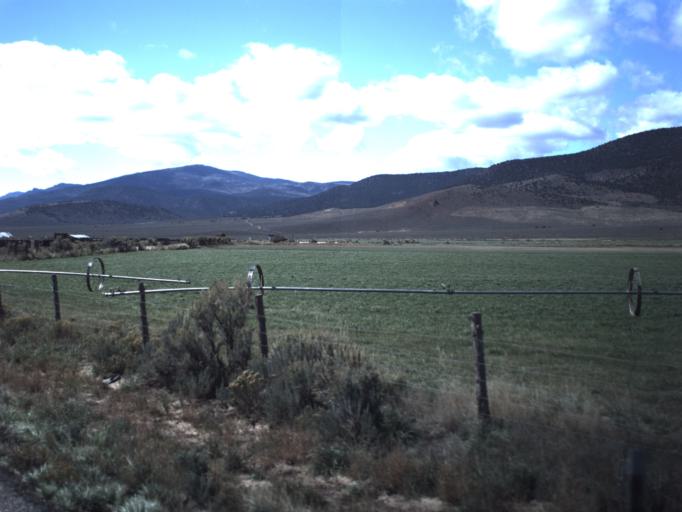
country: US
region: Utah
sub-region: Sevier County
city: Monroe
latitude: 38.4718
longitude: -111.9048
